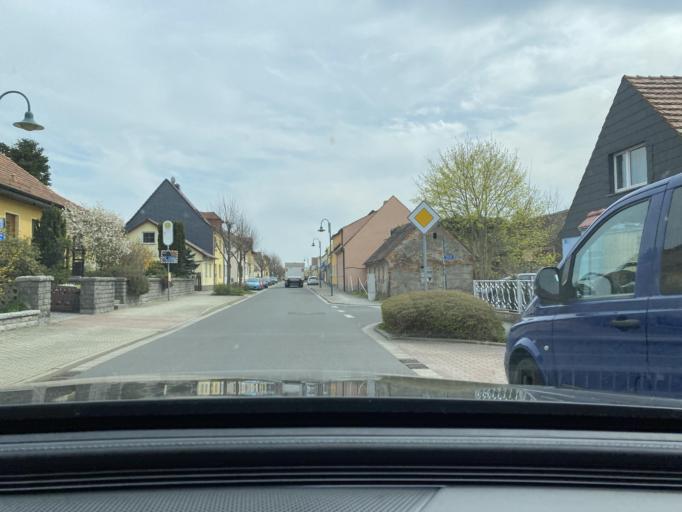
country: DE
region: Saxony
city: Wittichenau
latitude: 51.3819
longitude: 14.2500
